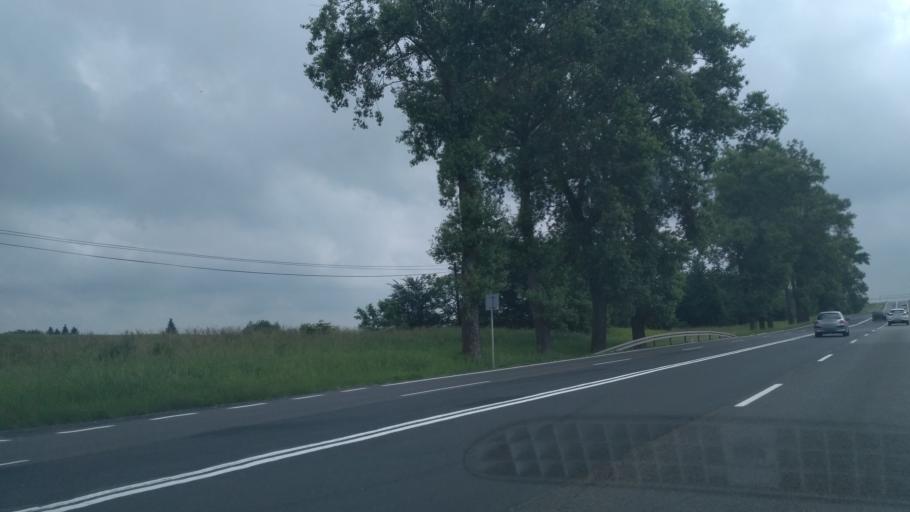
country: PL
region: Subcarpathian Voivodeship
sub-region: Powiat przeworski
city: Rozborz
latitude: 50.0513
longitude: 22.5237
